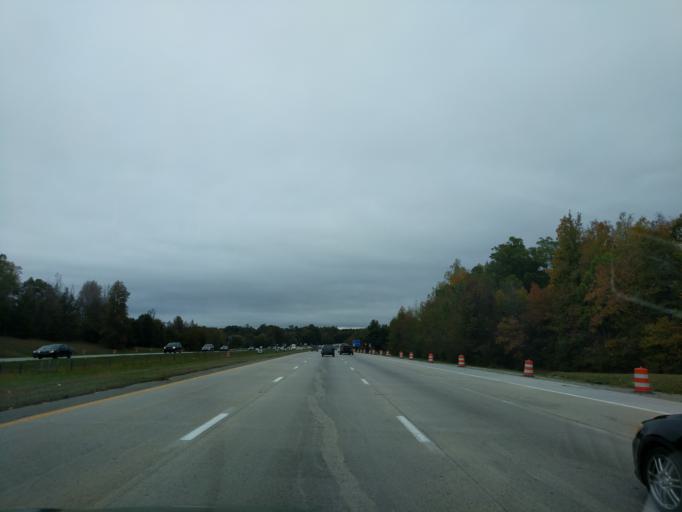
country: US
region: North Carolina
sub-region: Randolph County
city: Archdale
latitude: 35.9076
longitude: -79.9516
